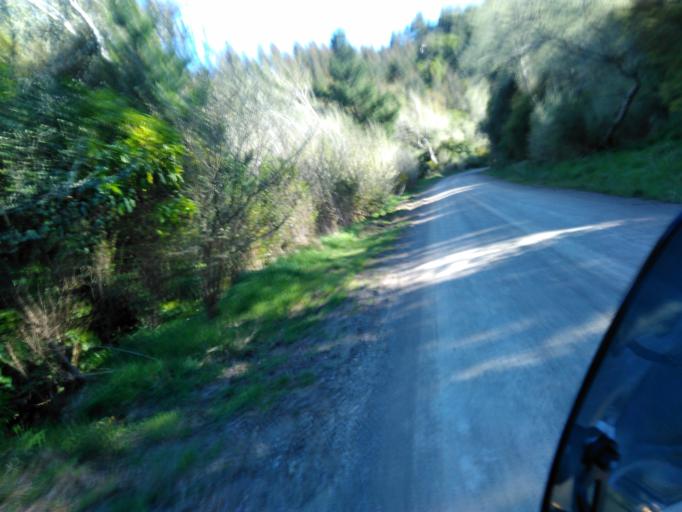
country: NZ
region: Gisborne
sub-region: Gisborne District
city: Gisborne
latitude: -38.4128
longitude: 177.6911
